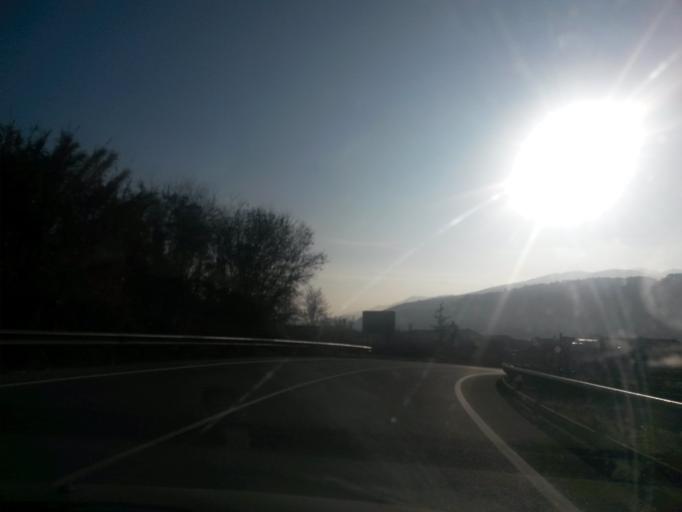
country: ES
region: Catalonia
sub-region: Provincia de Girona
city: Argelaguer
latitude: 42.2173
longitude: 2.6411
